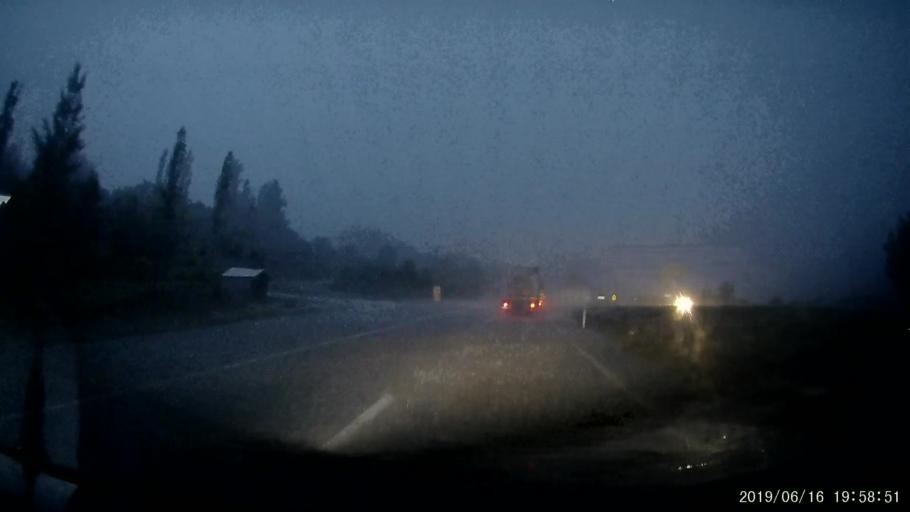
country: TR
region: Sivas
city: Koyulhisar
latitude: 40.2964
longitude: 37.7207
